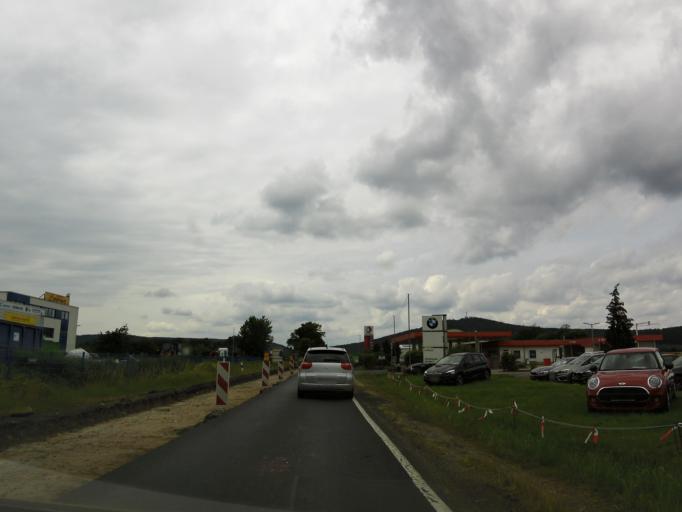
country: DE
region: Thuringia
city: Tiefenort
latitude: 50.8256
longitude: 10.1609
